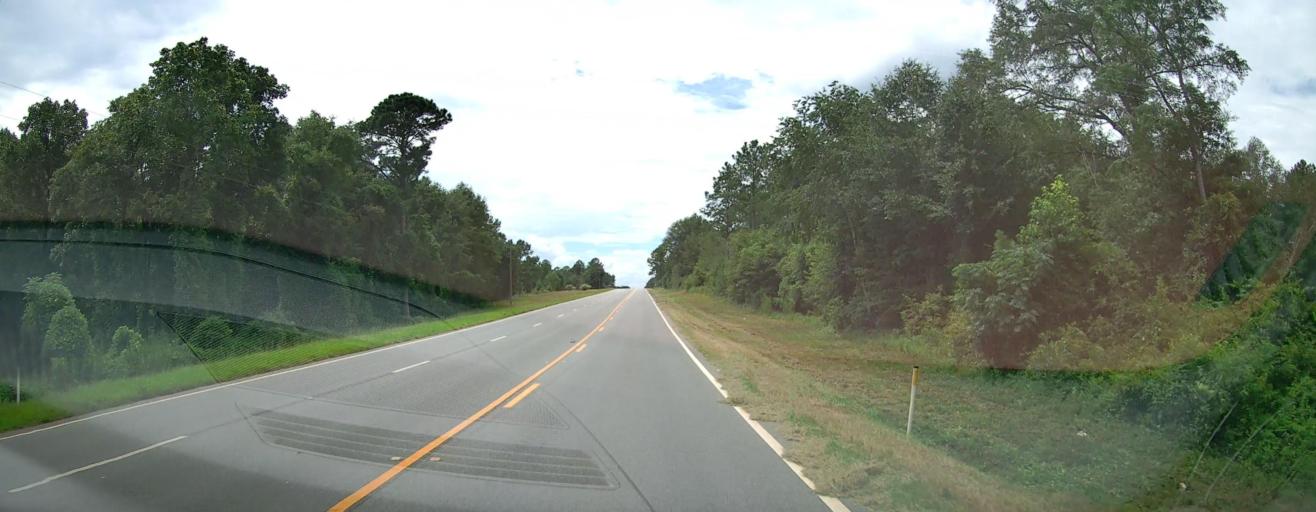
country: US
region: Georgia
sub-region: Macon County
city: Oglethorpe
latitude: 32.2822
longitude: -84.1487
